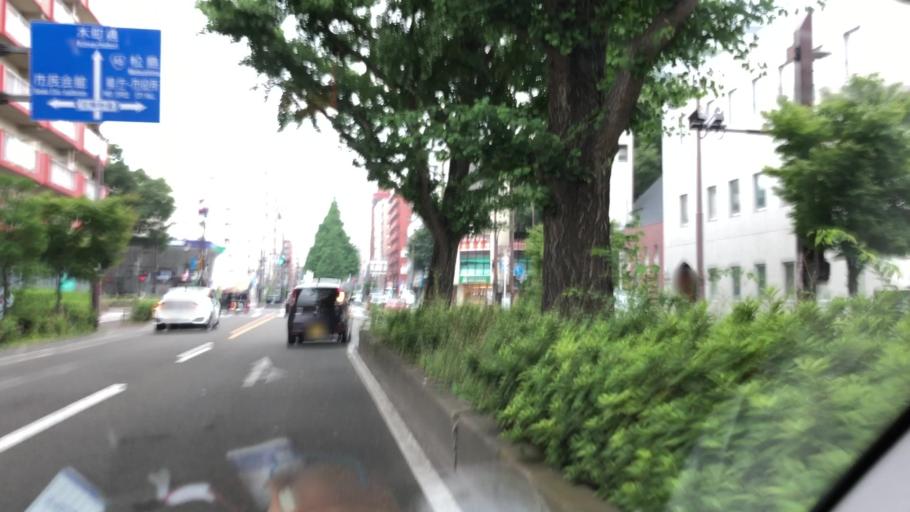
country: JP
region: Miyagi
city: Sendai-shi
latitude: 38.2643
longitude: 140.8671
